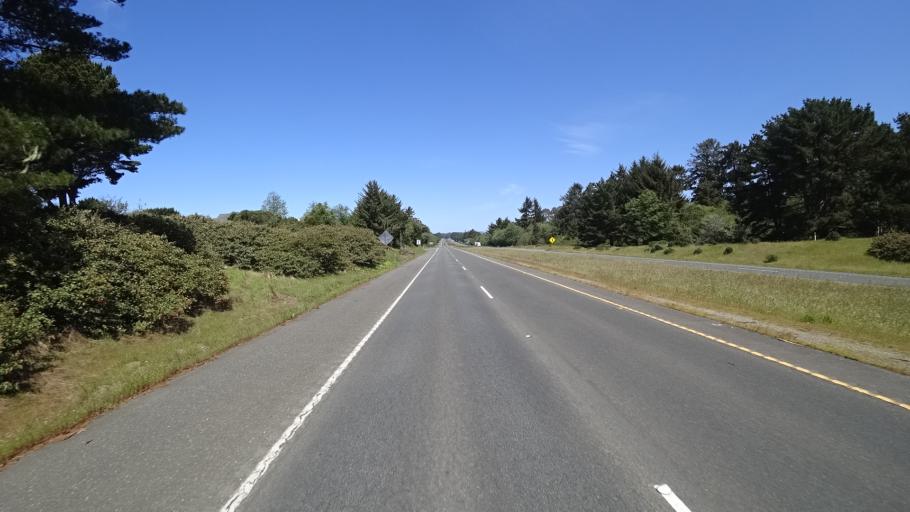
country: US
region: California
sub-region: Humboldt County
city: McKinleyville
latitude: 40.9570
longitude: -124.1163
